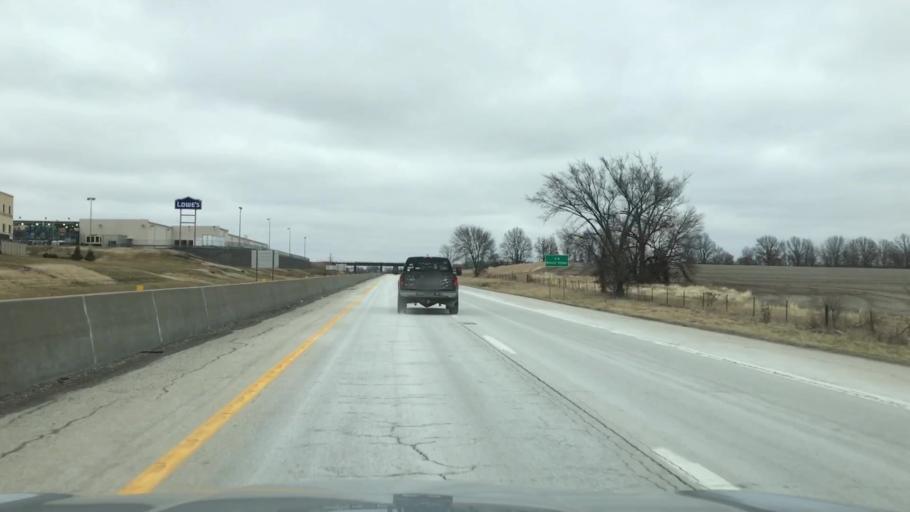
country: US
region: Missouri
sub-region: Livingston County
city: Chillicothe
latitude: 39.7732
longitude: -93.5471
